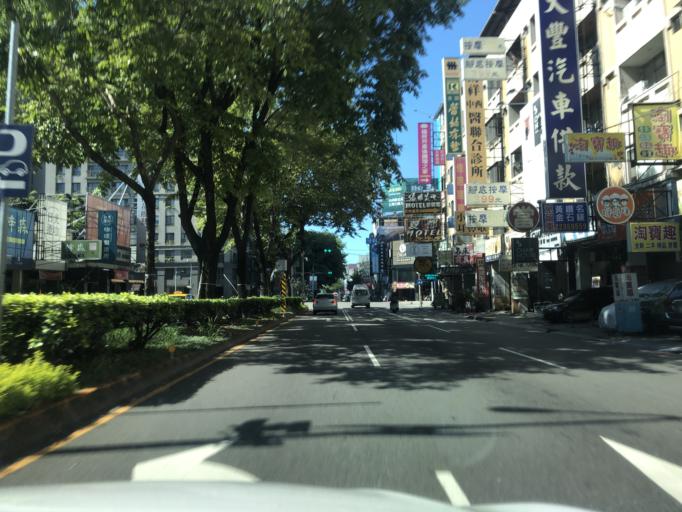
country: TW
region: Taiwan
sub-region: Taichung City
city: Taichung
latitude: 24.1660
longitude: 120.6850
